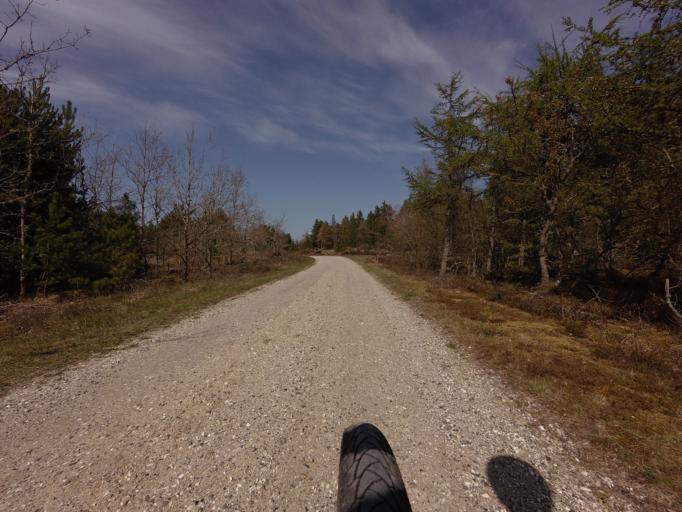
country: DK
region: North Denmark
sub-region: Jammerbugt Kommune
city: Brovst
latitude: 57.1978
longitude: 9.5394
